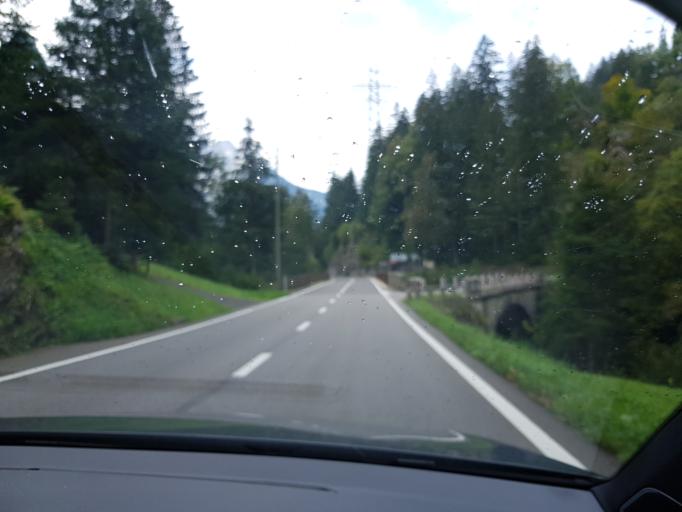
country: CH
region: Bern
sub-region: Interlaken-Oberhasli District
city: Meiringen
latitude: 46.7147
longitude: 8.2733
